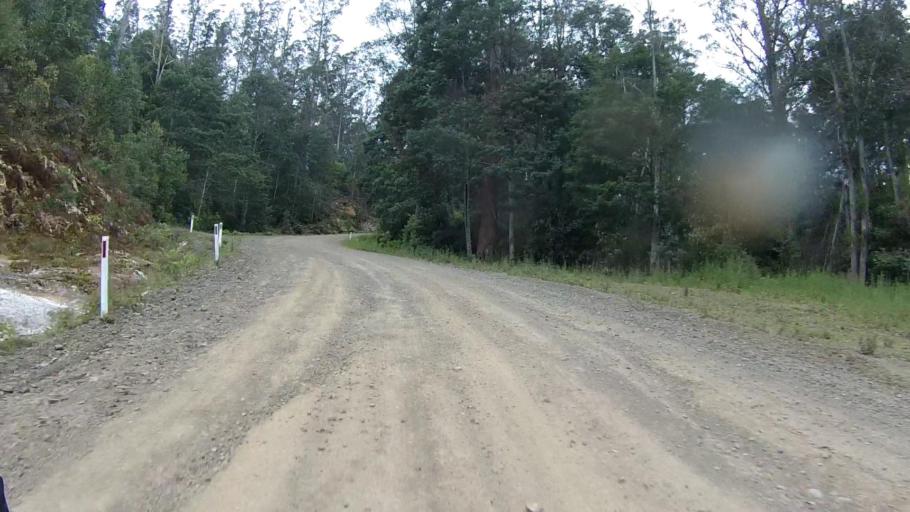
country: AU
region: Tasmania
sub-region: Sorell
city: Sorell
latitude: -42.7070
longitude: 147.8499
